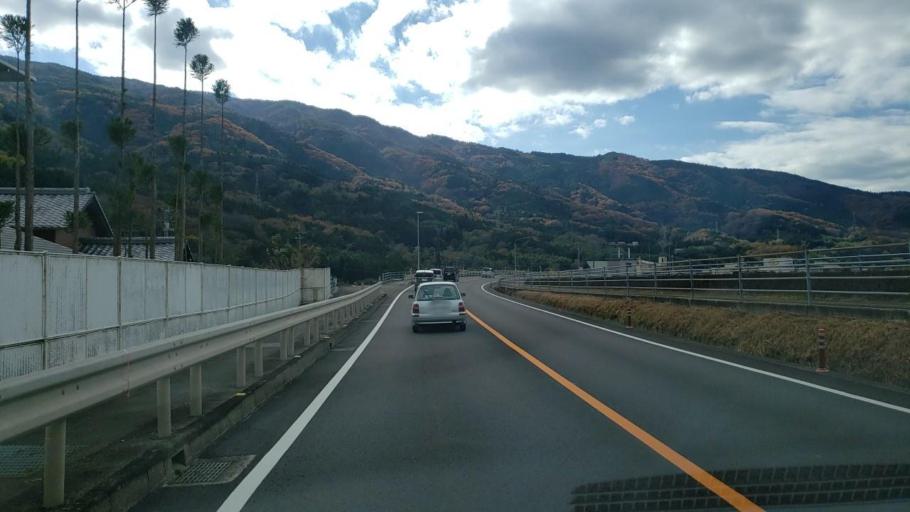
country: JP
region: Tokushima
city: Wakimachi
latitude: 34.0539
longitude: 134.1194
